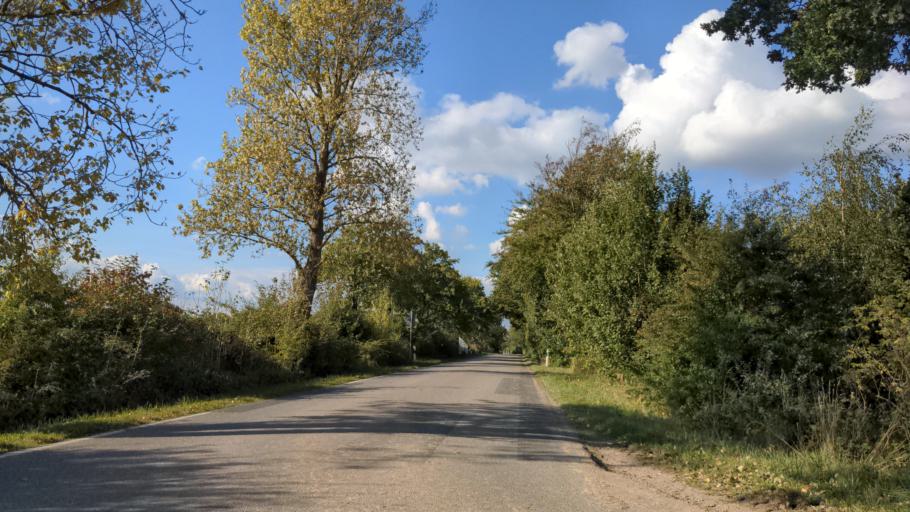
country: DE
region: Schleswig-Holstein
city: Monkhagen
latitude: 53.9139
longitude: 10.5529
